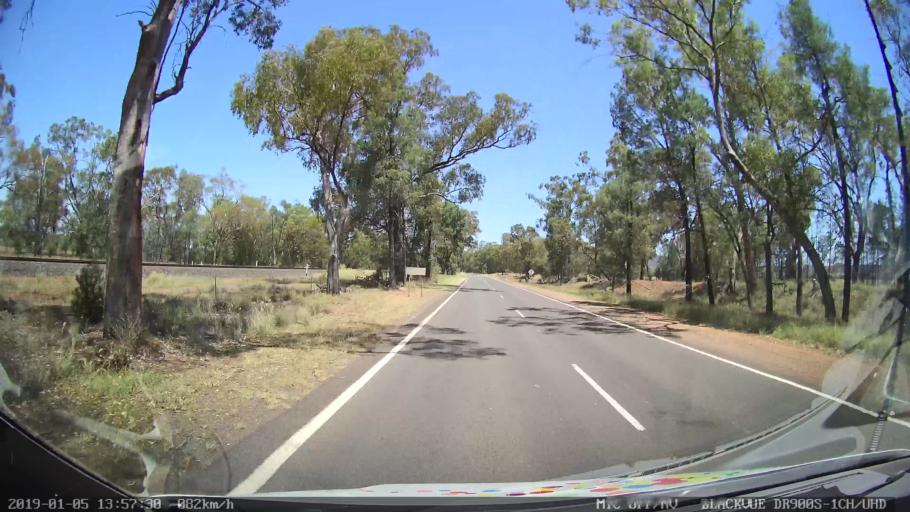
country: AU
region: New South Wales
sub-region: Gunnedah
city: Gunnedah
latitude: -31.1282
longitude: 150.2750
